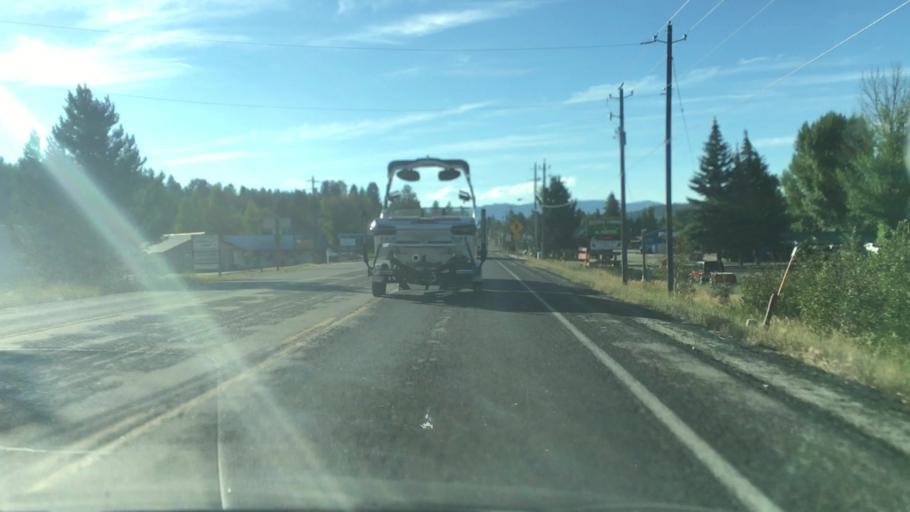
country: US
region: Idaho
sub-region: Valley County
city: Cascade
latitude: 44.5035
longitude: -116.0273
